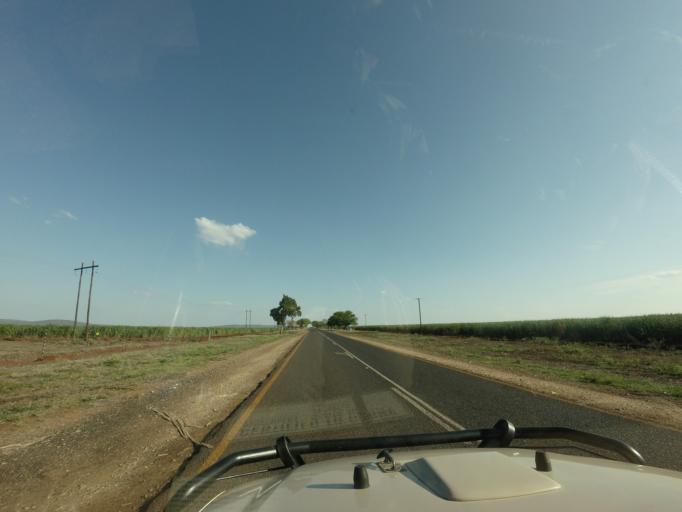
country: ZA
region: Mpumalanga
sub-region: Ehlanzeni District
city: Komatipoort
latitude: -25.3919
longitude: 31.9148
